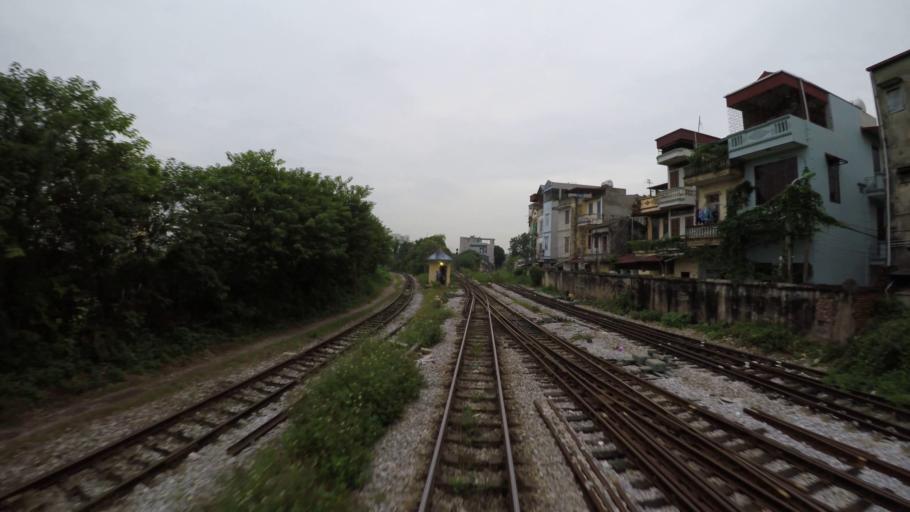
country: VN
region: Ha Noi
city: Trau Quy
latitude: 21.0234
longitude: 105.9310
